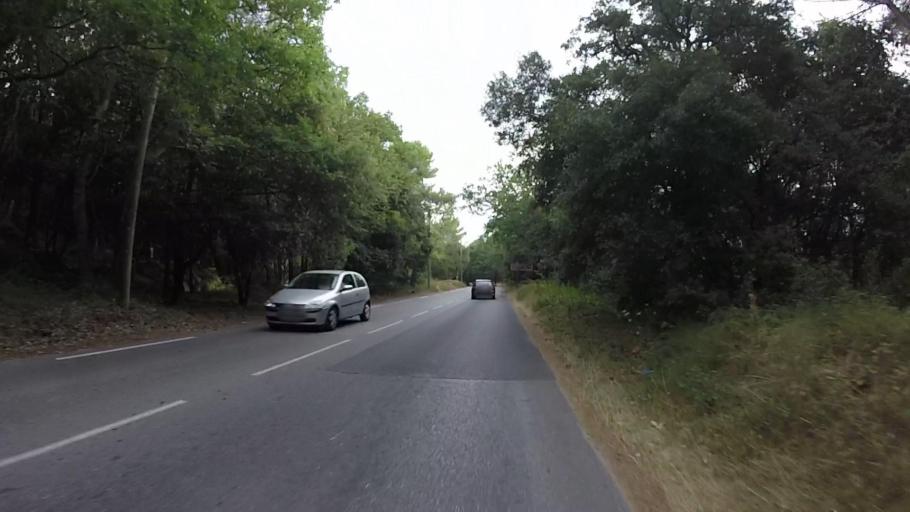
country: FR
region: Provence-Alpes-Cote d'Azur
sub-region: Departement des Alpes-Maritimes
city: Vallauris
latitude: 43.5962
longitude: 7.0370
